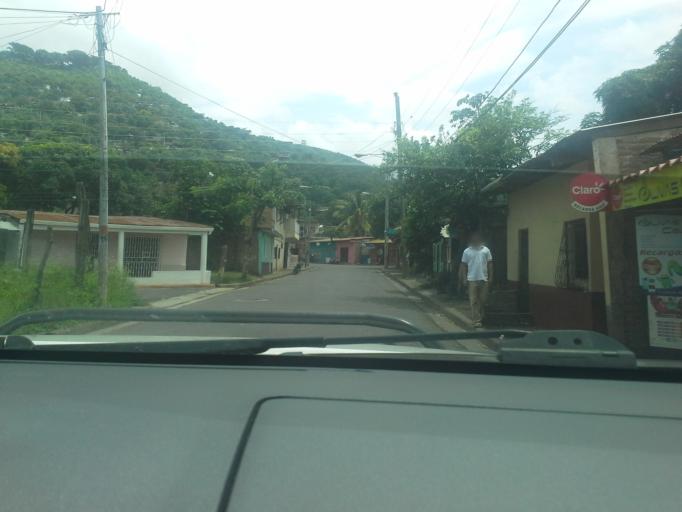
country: NI
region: Matagalpa
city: Matagalpa
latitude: 12.9208
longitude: -85.9274
